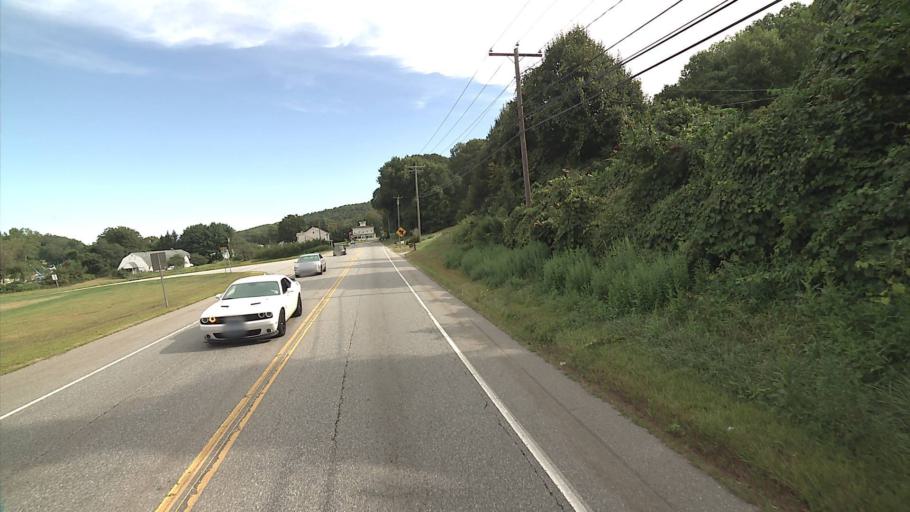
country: US
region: Connecticut
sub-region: New London County
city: Baltic
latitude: 41.5895
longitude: -72.1303
